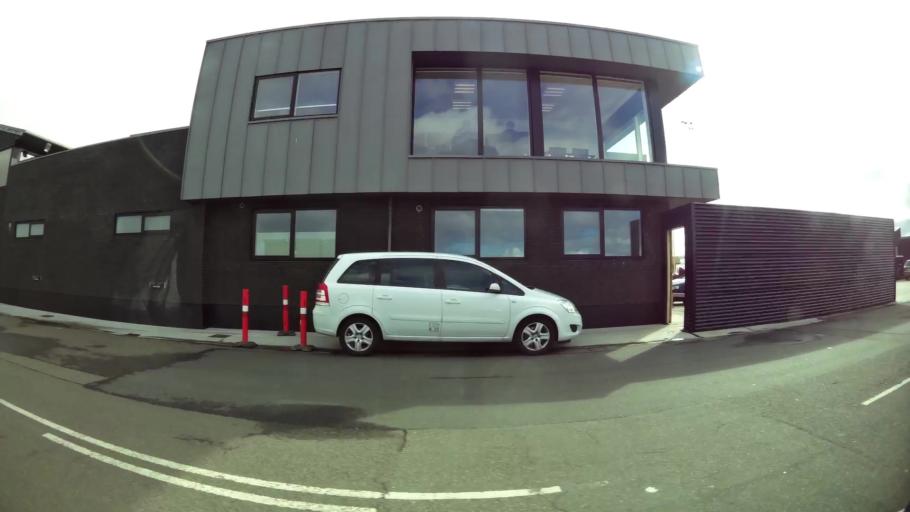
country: DK
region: South Denmark
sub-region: Fano Kommune
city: Nordby
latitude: 55.4784
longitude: 8.4106
